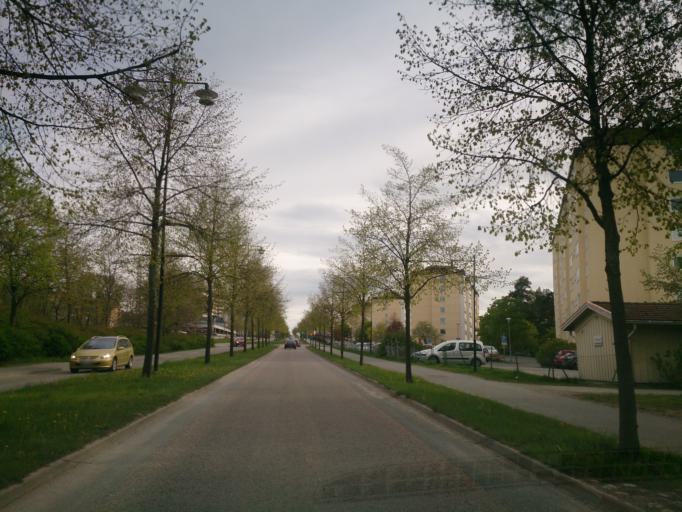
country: SE
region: Stockholm
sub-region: Haninge Kommun
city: Handen
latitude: 59.1736
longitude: 18.1399
